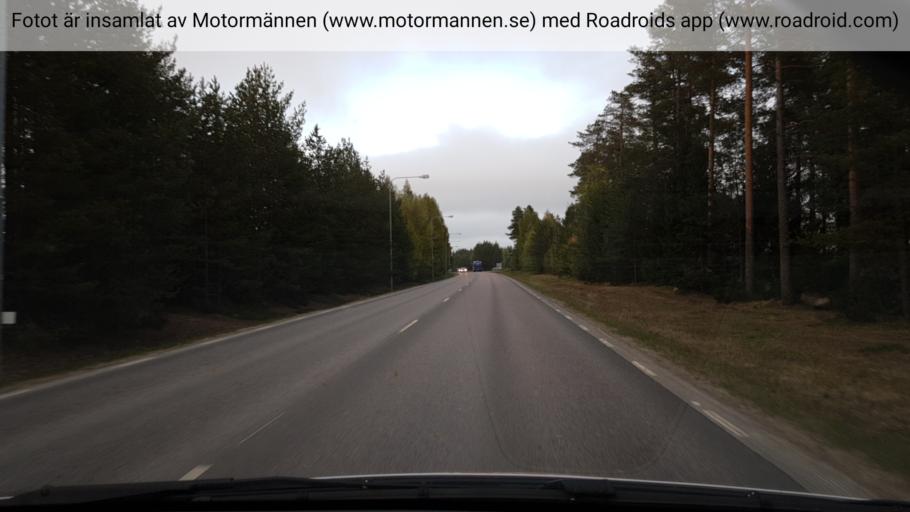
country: SE
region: Vaesterbotten
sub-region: Umea Kommun
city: Roback
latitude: 63.8103
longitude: 20.1797
